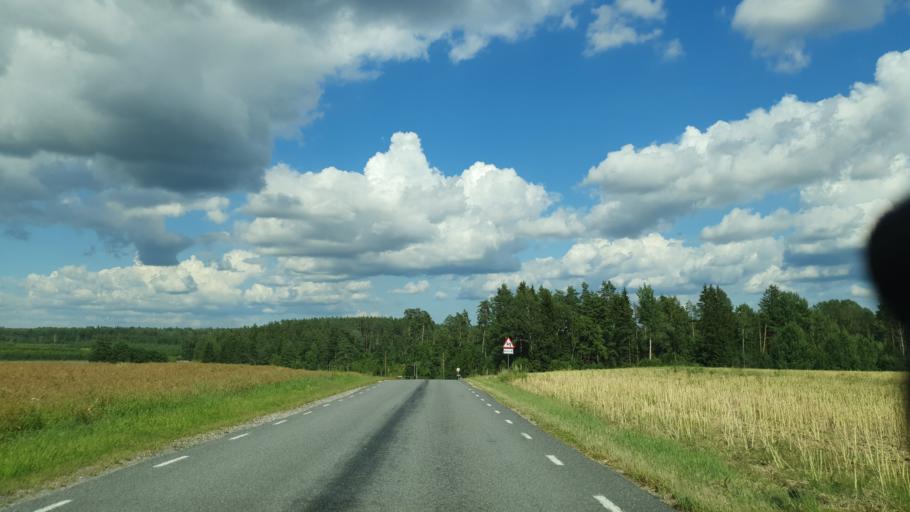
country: EE
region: Jogevamaa
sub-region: Tabivere vald
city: Tabivere
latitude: 58.6265
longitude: 26.5853
